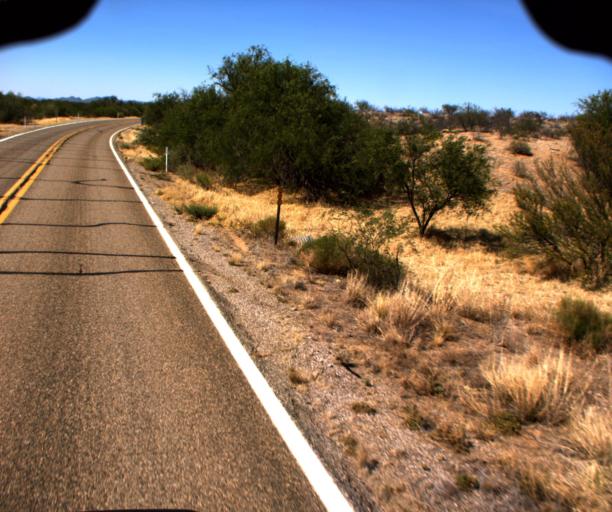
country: US
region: Arizona
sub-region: Pima County
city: Three Points
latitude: 31.9411
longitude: -111.3909
